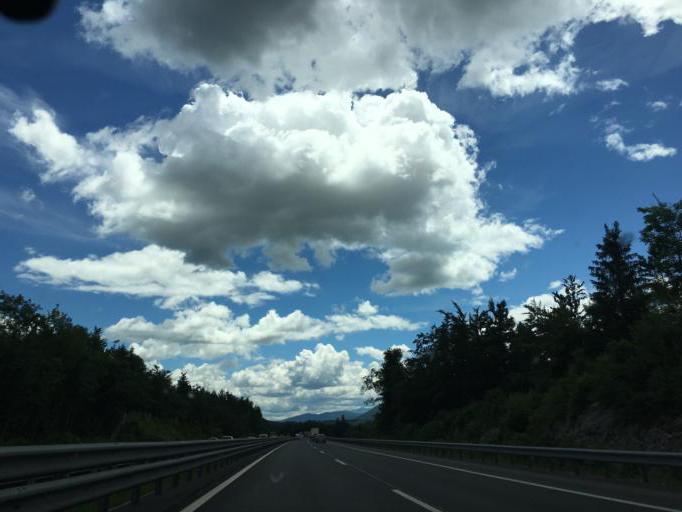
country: SI
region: Cerknica
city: Rakek
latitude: 45.8517
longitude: 14.2831
